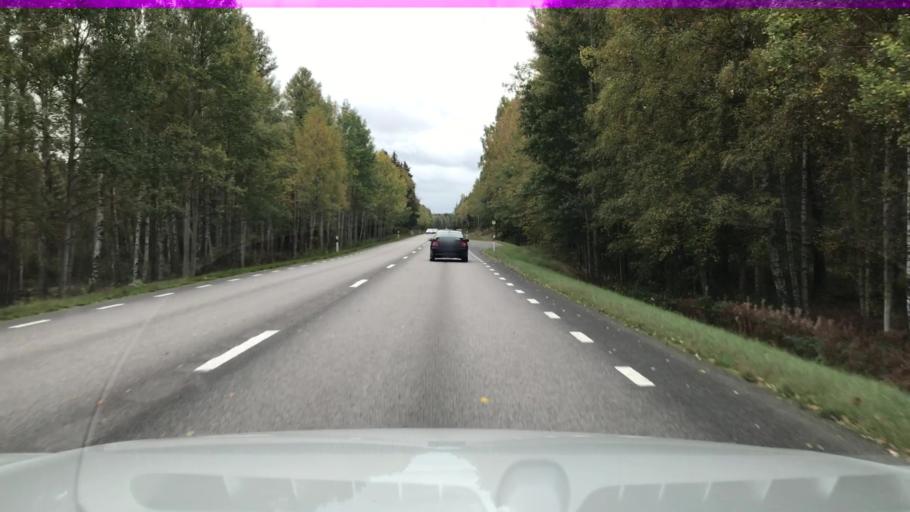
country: SE
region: Kalmar
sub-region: Hultsfreds Kommun
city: Hultsfred
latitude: 57.5504
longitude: 15.8453
